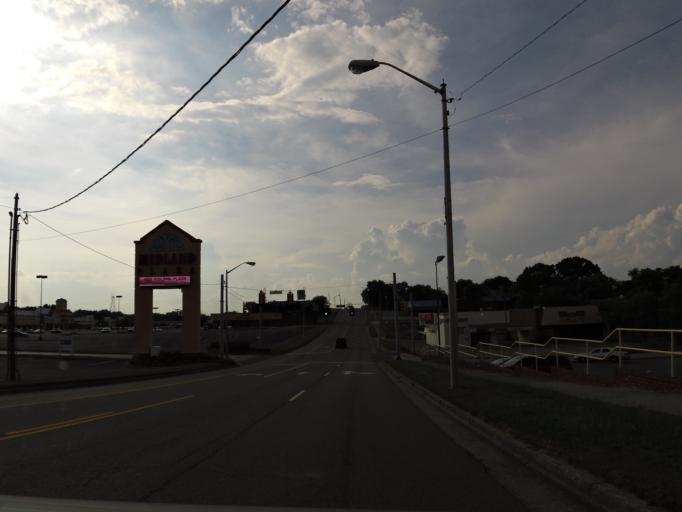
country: US
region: Tennessee
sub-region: Blount County
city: Maryville
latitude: 35.7611
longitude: -83.9768
